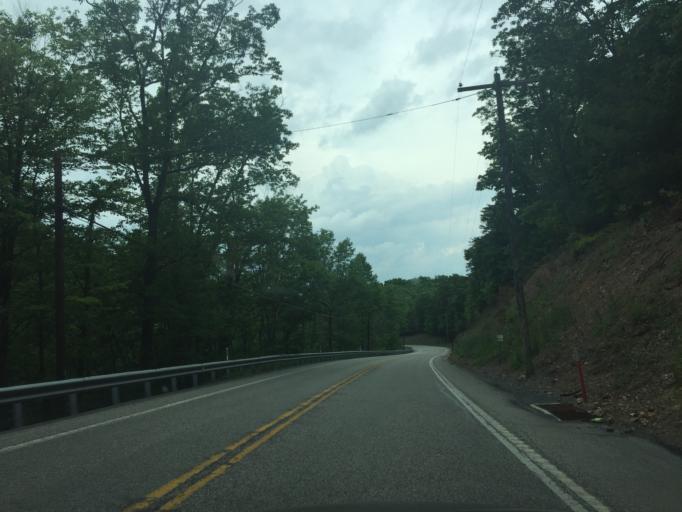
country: US
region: Pennsylvania
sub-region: Fulton County
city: McConnellsburg
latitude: 40.0406
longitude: -77.9659
